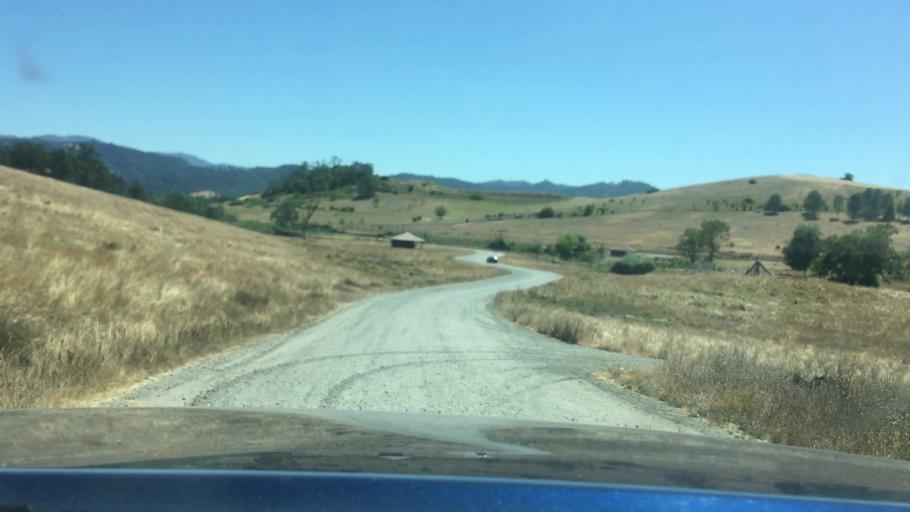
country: US
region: Oregon
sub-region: Douglas County
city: Winston
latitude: 43.1341
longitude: -123.4325
